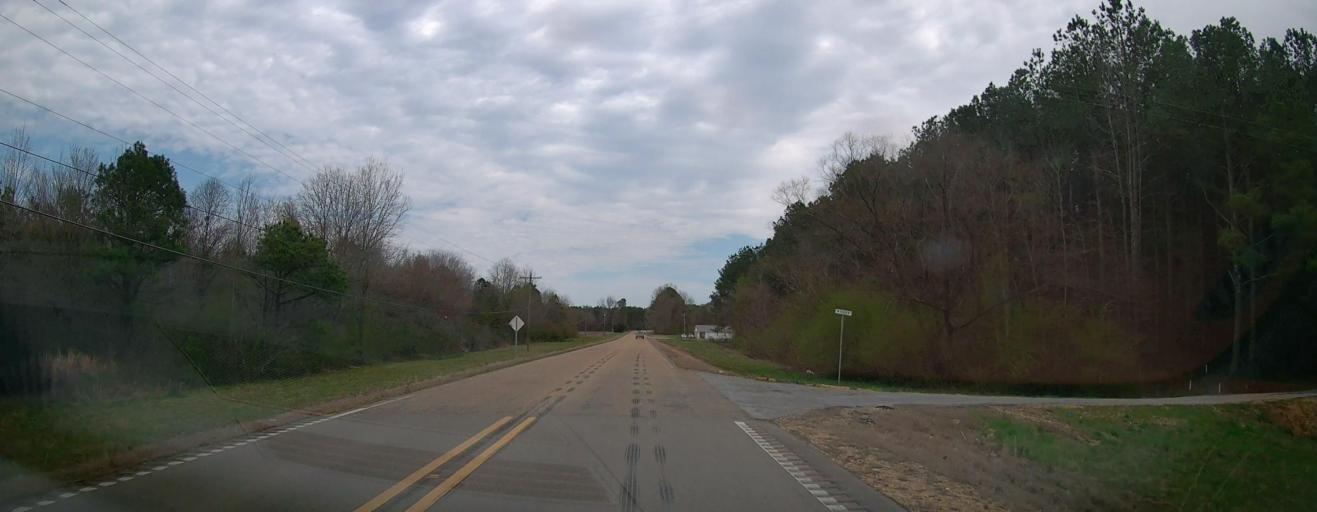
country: US
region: Mississippi
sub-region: Itawamba County
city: Fulton
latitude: 34.2312
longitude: -88.2457
